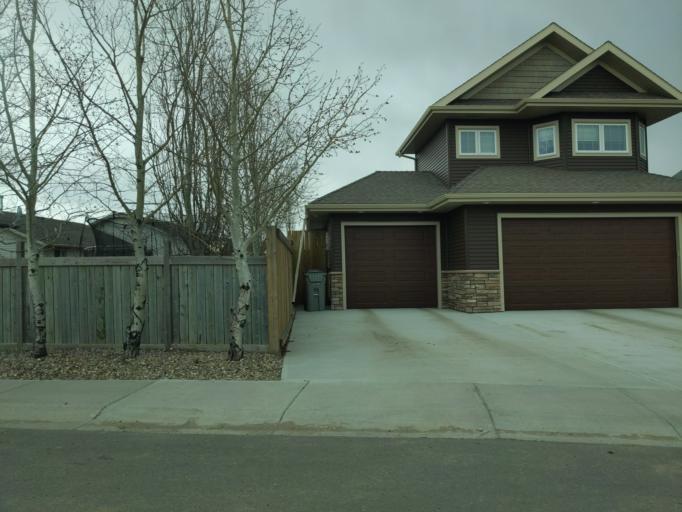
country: CA
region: Saskatchewan
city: Lloydminster
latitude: 53.2558
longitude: -110.0389
